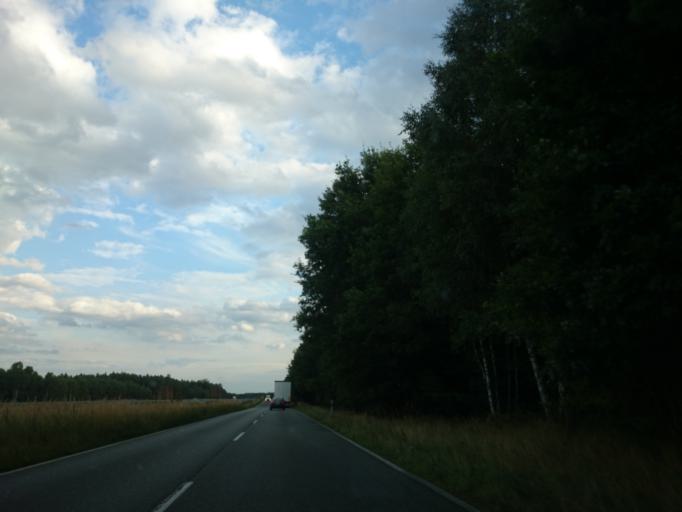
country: PL
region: West Pomeranian Voivodeship
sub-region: Powiat mysliborski
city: Nowogrodek Pomorski
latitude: 52.8264
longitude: 15.0702
